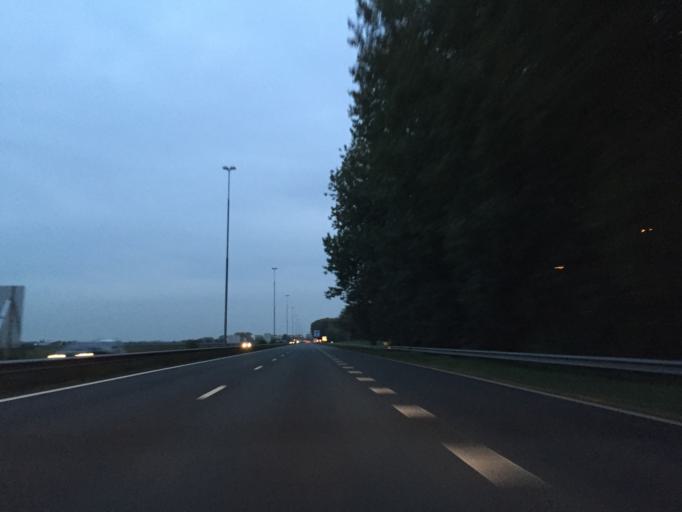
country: NL
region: North Brabant
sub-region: Gemeente Waalwijk
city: Waalwijk
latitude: 51.6942
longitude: 5.0802
